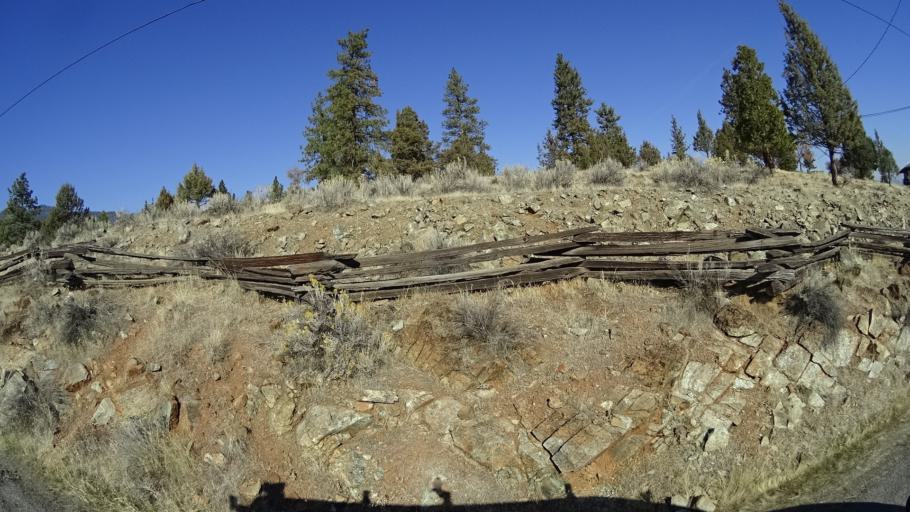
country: US
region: California
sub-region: Siskiyou County
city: Yreka
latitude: 41.7285
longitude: -122.6553
